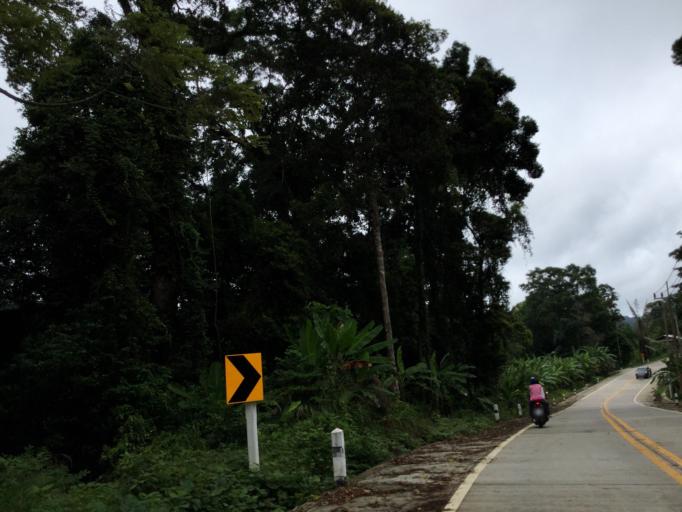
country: TH
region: Nakhon Si Thammarat
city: Ko Pha Ngan
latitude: 9.7276
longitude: 100.0455
